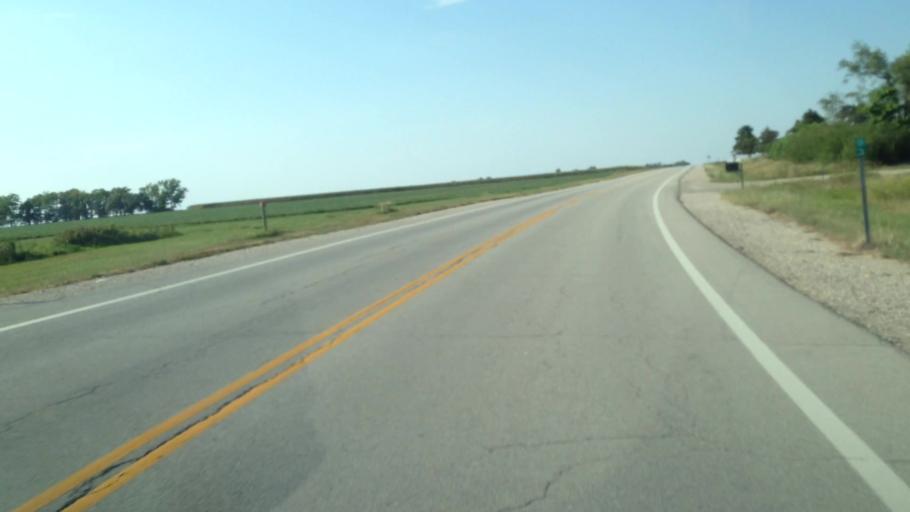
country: US
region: Kansas
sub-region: Anderson County
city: Garnett
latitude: 38.0857
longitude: -95.2433
